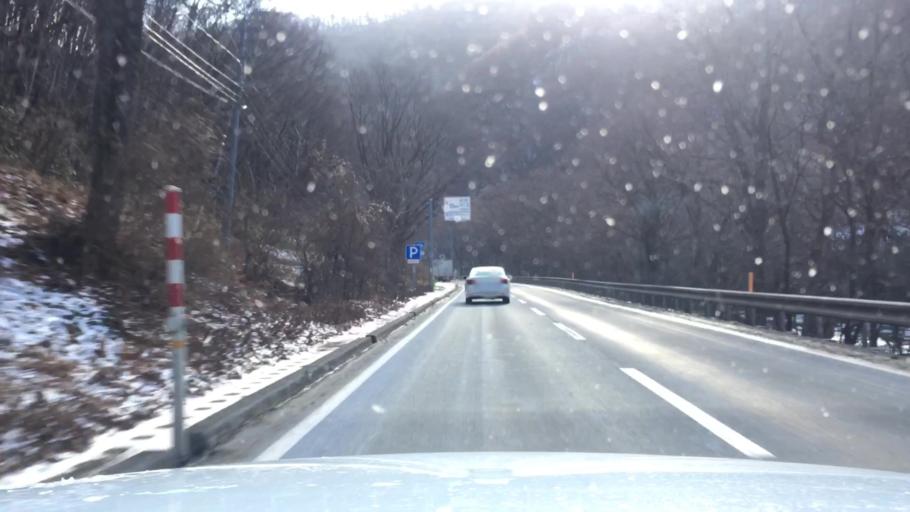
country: JP
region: Iwate
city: Tono
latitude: 39.6180
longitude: 141.4970
